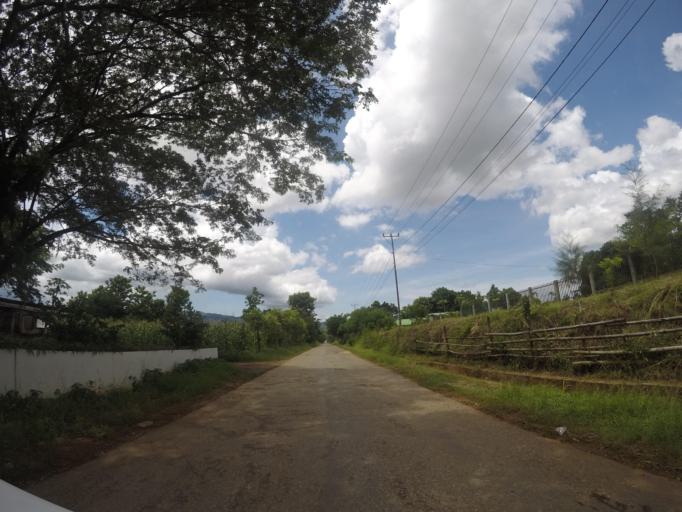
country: TL
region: Bobonaro
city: Maliana
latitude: -8.9741
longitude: 125.1382
